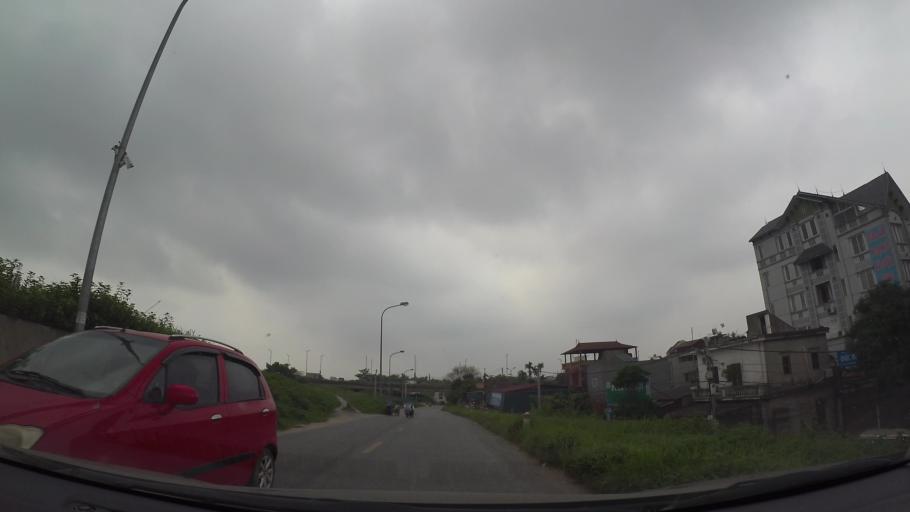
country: VN
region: Ha Noi
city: Trau Quy
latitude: 21.0394
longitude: 105.9356
